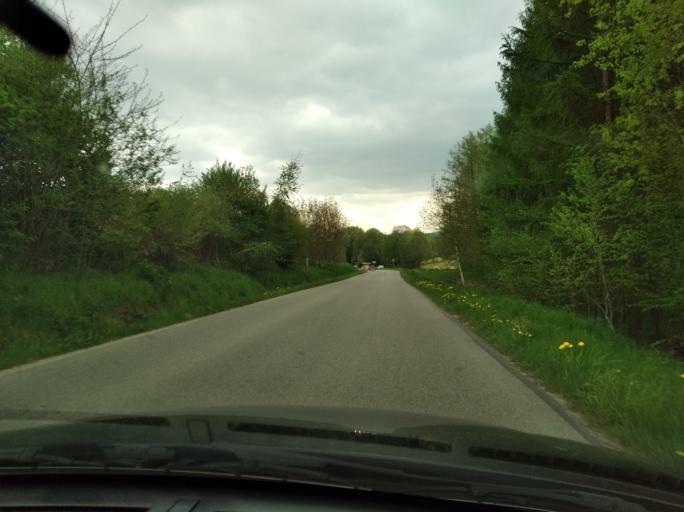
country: PL
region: Subcarpathian Voivodeship
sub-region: Powiat debicki
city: Leki Gorne
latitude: 49.9798
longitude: 21.1577
